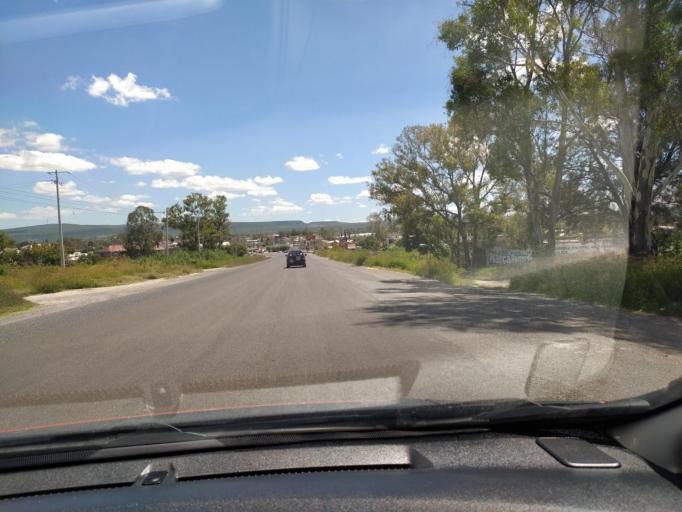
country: MX
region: Jalisco
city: San Diego de Alejandria
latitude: 20.9975
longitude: -101.9970
